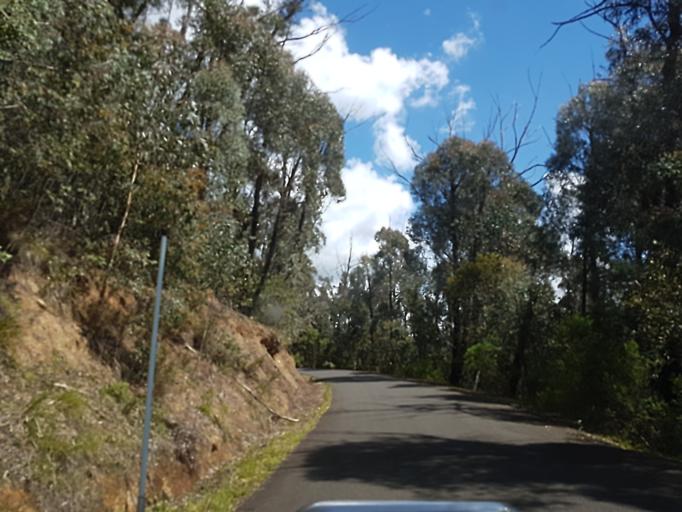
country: AU
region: Victoria
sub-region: East Gippsland
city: Bairnsdale
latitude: -37.3904
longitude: 147.2390
